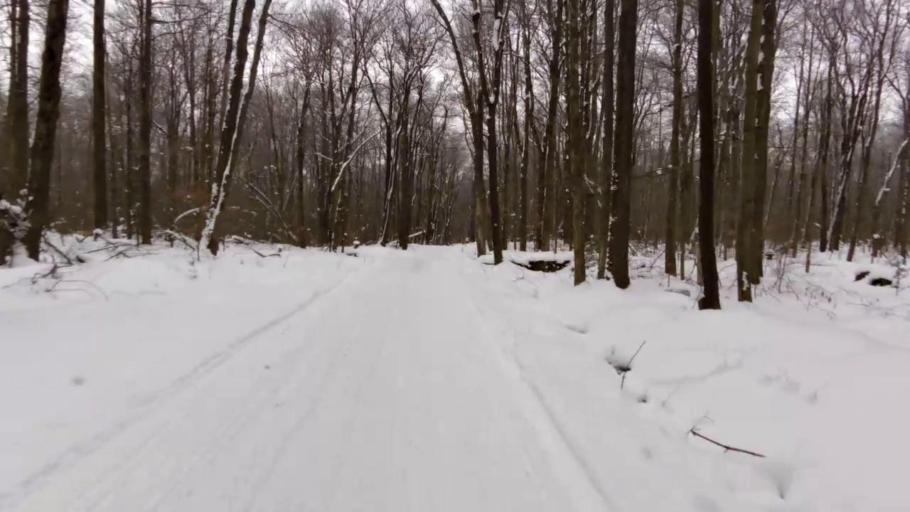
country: US
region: Pennsylvania
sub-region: McKean County
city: Bradford
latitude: 42.0065
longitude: -78.7203
